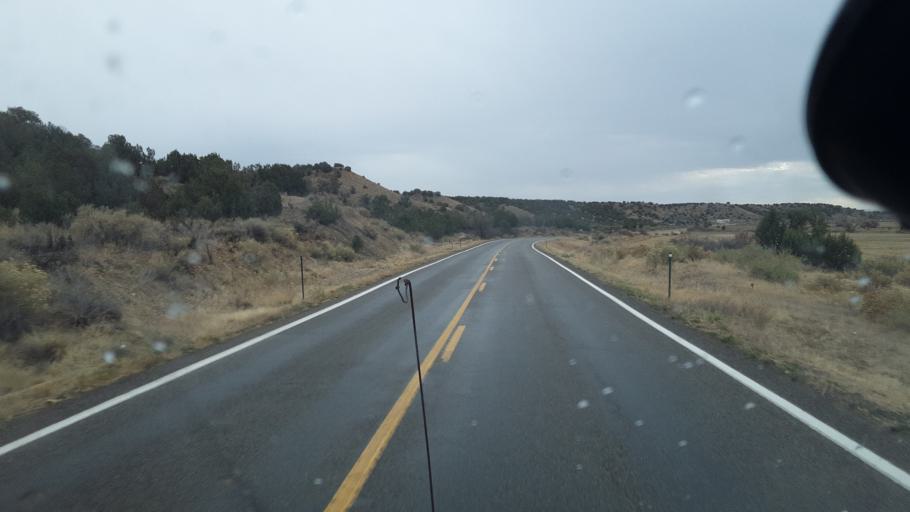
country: US
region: New Mexico
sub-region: San Juan County
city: Spencerville
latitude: 37.0171
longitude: -108.1832
